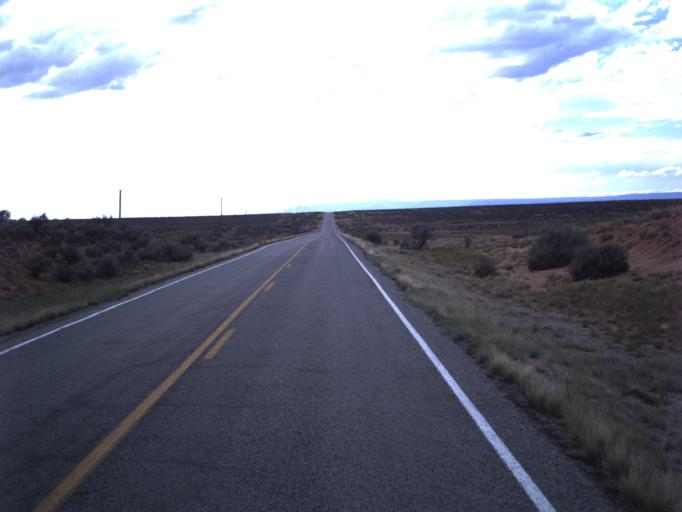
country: US
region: Utah
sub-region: San Juan County
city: Blanding
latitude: 37.4256
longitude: -109.3482
